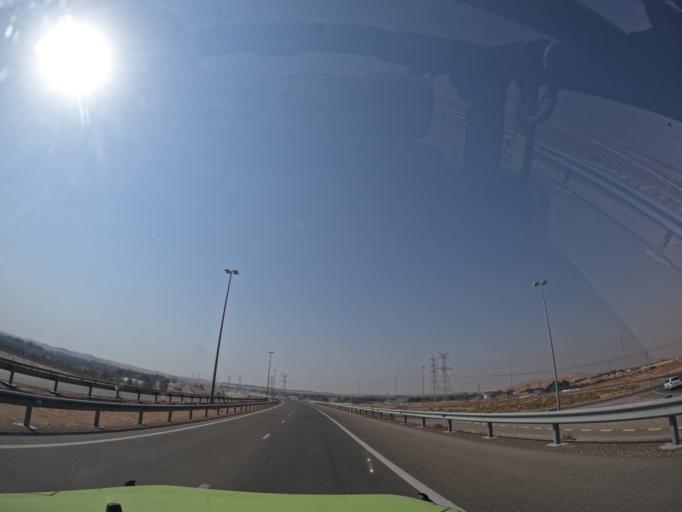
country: OM
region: Al Buraimi
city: Al Buraymi
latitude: 24.3702
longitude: 55.7283
